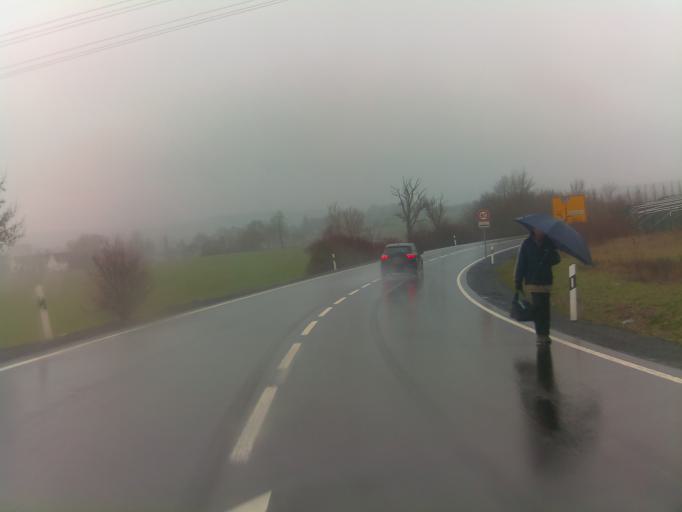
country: DE
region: Thuringia
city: Eisfeld
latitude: 50.4401
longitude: 10.9100
